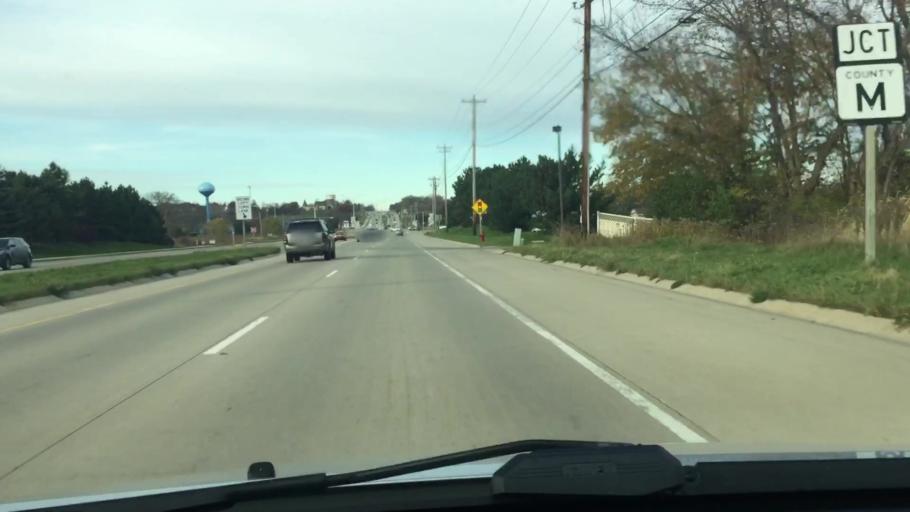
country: US
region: Wisconsin
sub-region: Waukesha County
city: Pewaukee
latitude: 43.0656
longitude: -88.2250
